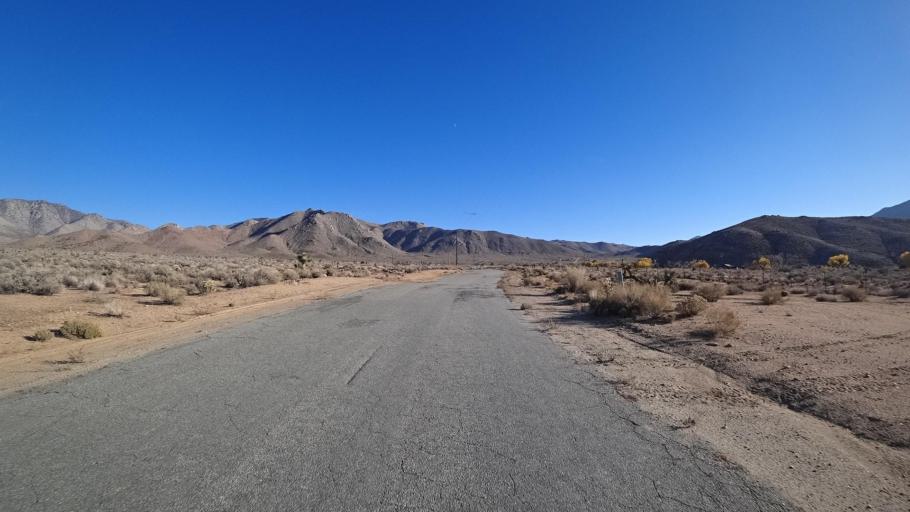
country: US
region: California
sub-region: Kern County
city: Weldon
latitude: 35.5518
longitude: -118.2129
